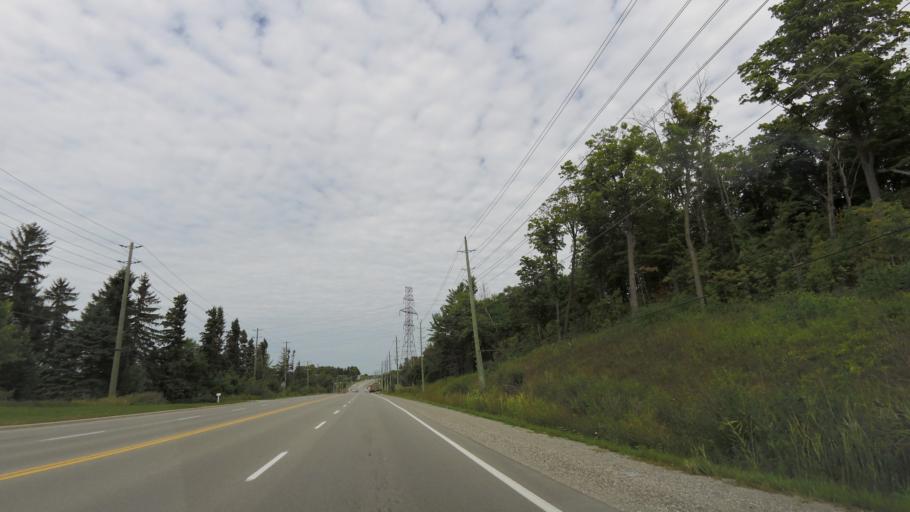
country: CA
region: Ontario
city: Newmarket
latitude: 44.0519
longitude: -79.5068
